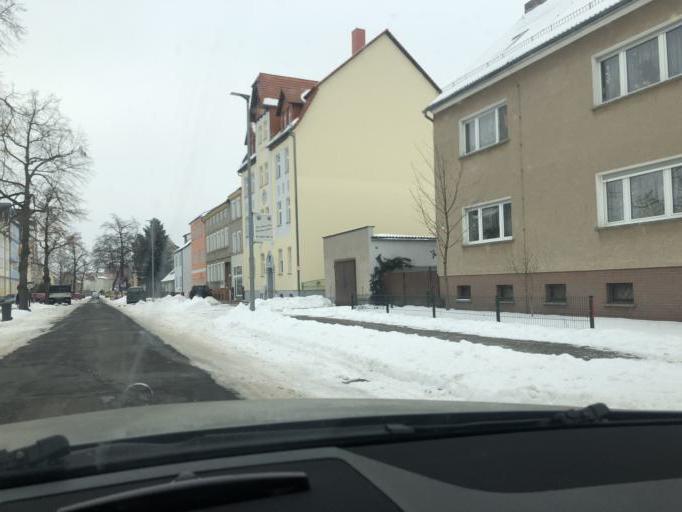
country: DE
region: Brandenburg
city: Guben
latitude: 51.9444
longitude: 14.7086
